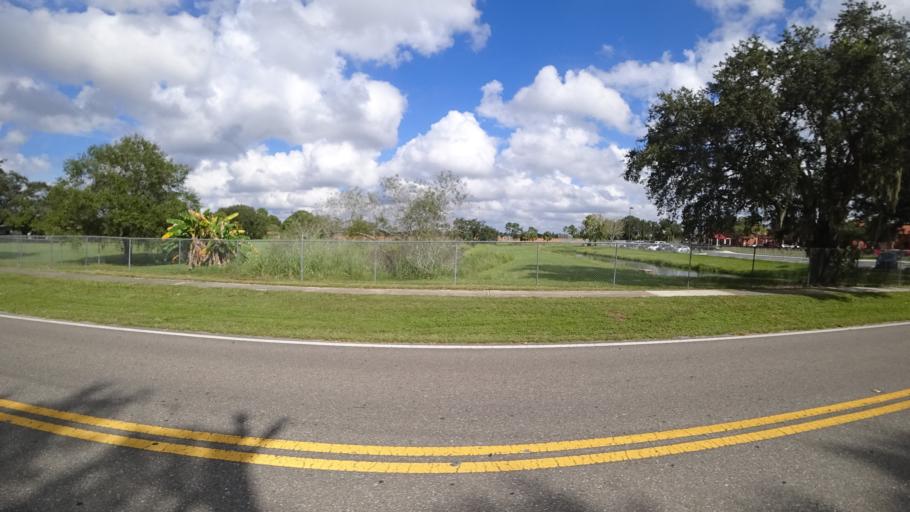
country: US
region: Florida
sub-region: Manatee County
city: Samoset
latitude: 27.4769
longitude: -82.5394
